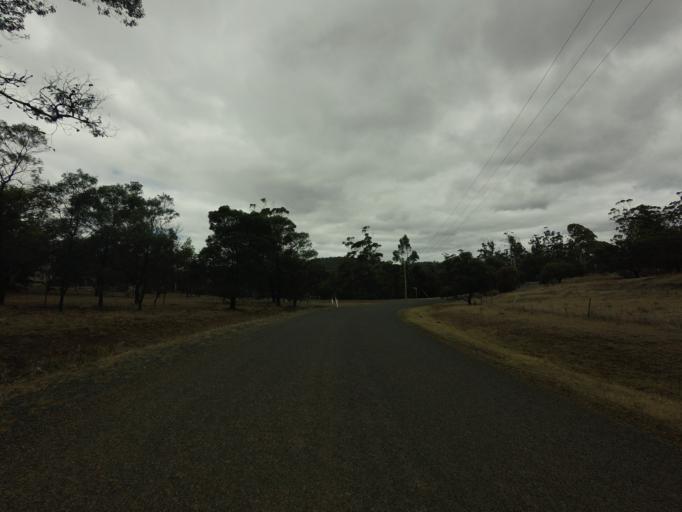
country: AU
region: Tasmania
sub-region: Clarence
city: Cambridge
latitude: -42.7908
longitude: 147.4025
